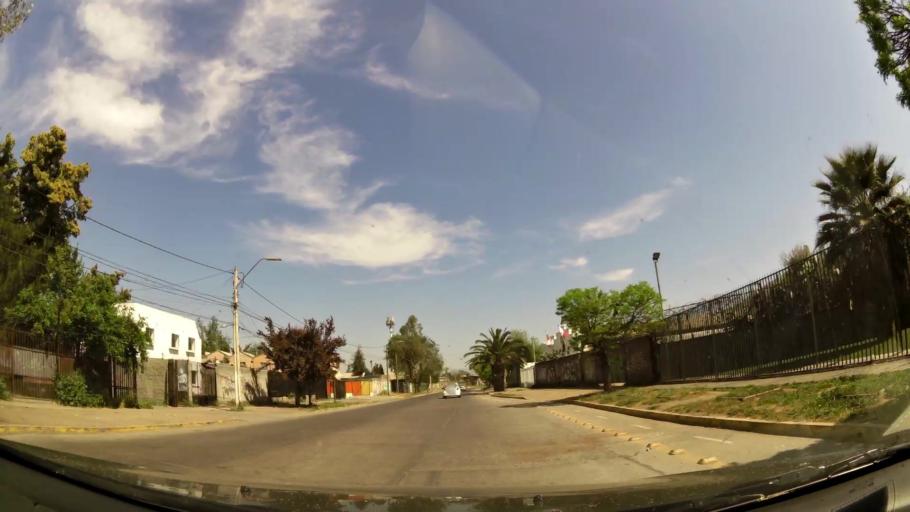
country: CL
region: Santiago Metropolitan
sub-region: Provincia de Santiago
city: Lo Prado
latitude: -33.4017
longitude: -70.7223
